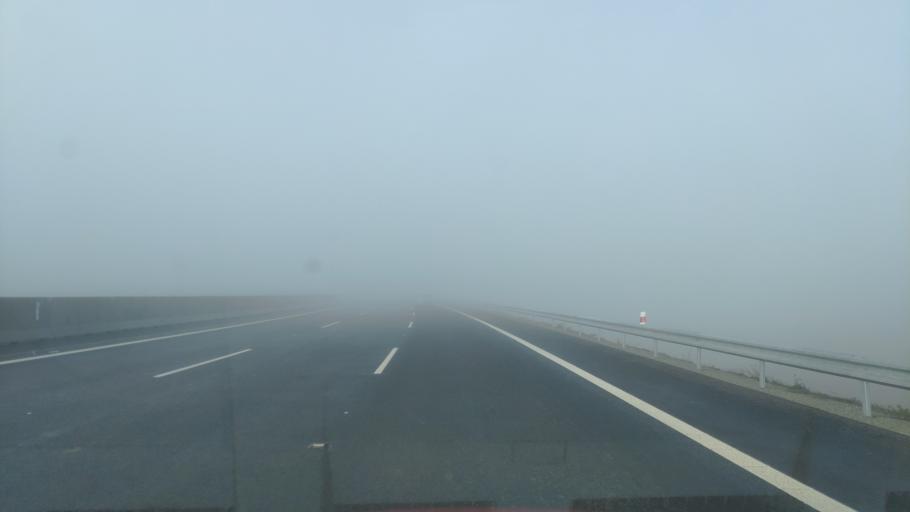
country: SK
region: Kosicky
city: Kosice
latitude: 48.7312
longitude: 21.4045
